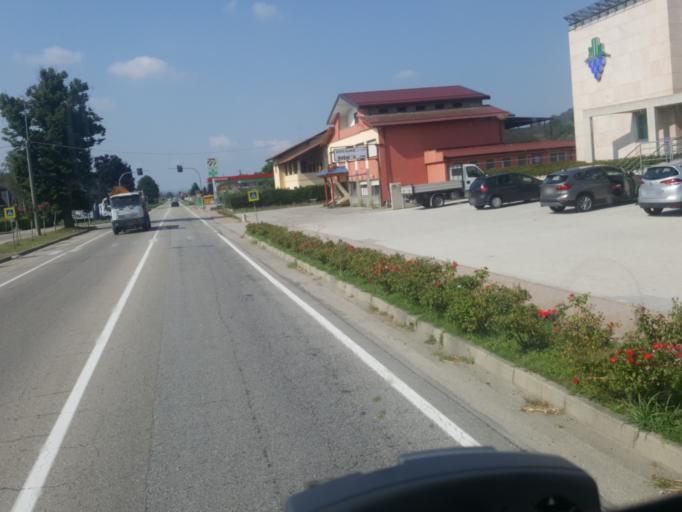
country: IT
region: Piedmont
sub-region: Provincia di Cuneo
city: Sant'Antonio
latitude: 44.7450
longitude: 8.0598
